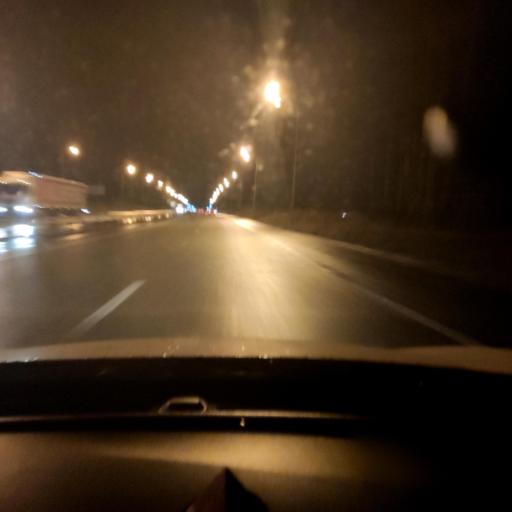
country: RU
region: Tatarstan
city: Osinovo
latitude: 55.8299
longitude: 48.8493
